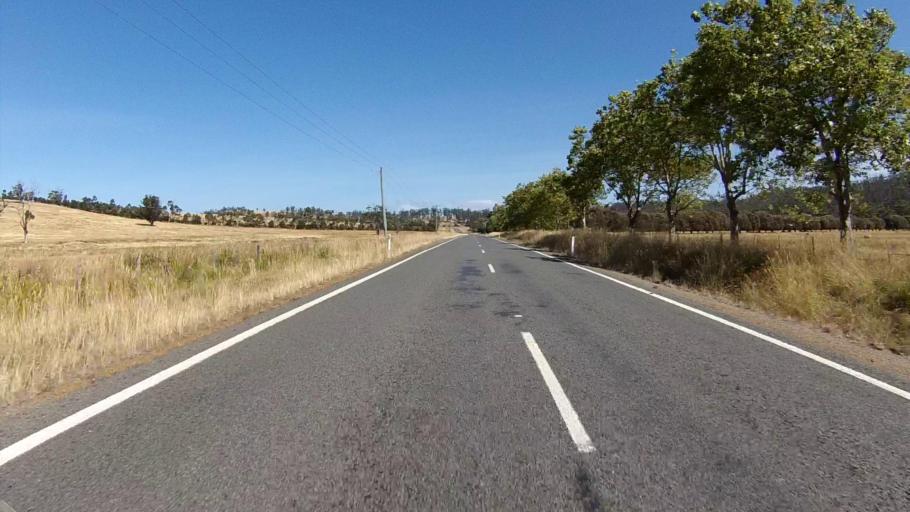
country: AU
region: Tasmania
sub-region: Sorell
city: Sorell
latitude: -42.4595
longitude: 147.9261
